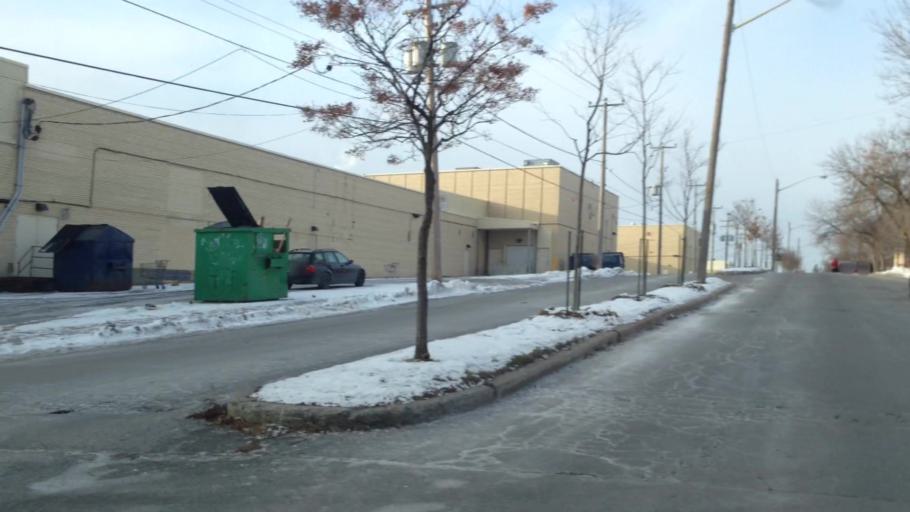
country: CA
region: Quebec
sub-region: Laval
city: Laval
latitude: 45.5423
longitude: -73.7476
